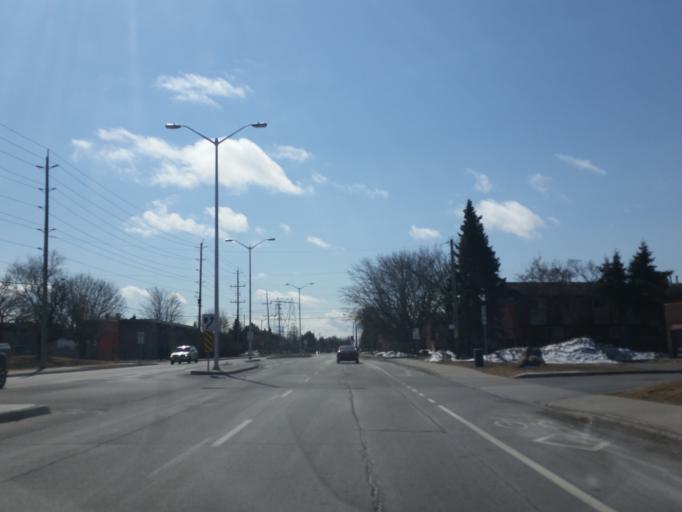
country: CA
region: Ontario
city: Bells Corners
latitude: 45.3214
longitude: -75.8330
